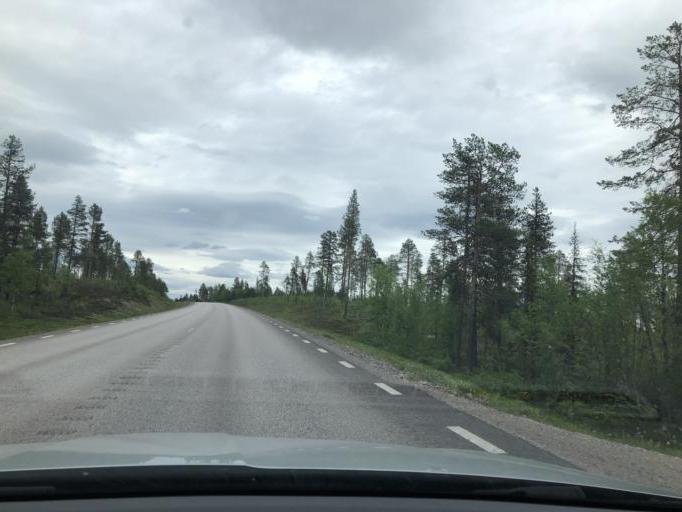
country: SE
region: Norrbotten
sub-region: Gallivare Kommun
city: Malmberget
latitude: 67.6539
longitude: 21.2028
